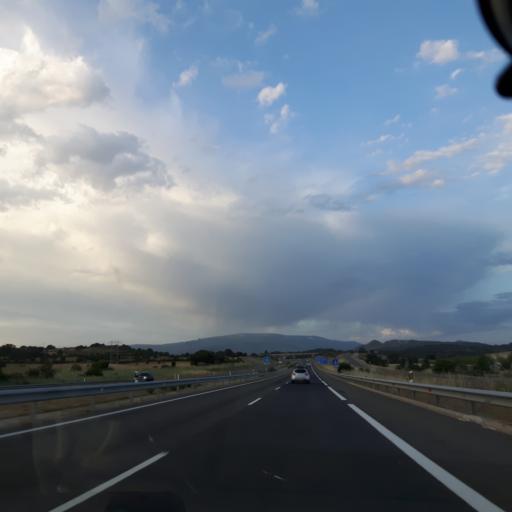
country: ES
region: Castille and Leon
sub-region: Provincia de Salamanca
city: Fuentes de Bejar
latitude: 40.5112
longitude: -5.6744
